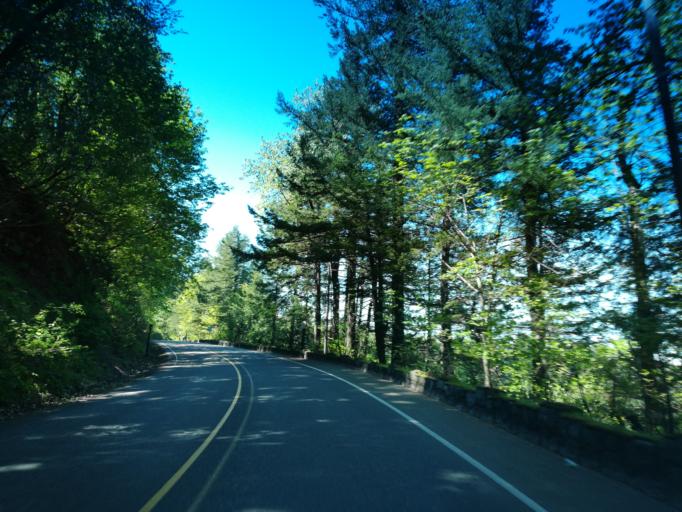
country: US
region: Oregon
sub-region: Multnomah County
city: Troutdale
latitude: 45.5104
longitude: -122.3697
